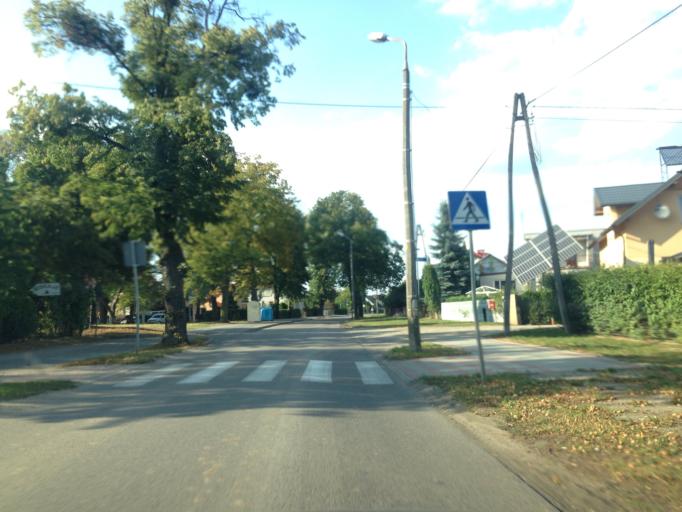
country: PL
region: Warmian-Masurian Voivodeship
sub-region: Powiat ilawski
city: Ilawa
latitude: 53.6151
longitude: 19.5683
